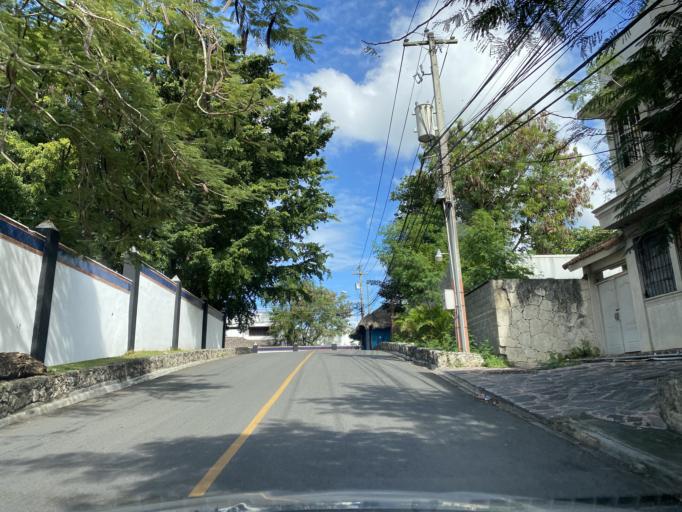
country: DO
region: Santo Domingo
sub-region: Santo Domingo
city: Boca Chica
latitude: 18.4490
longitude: -69.6034
